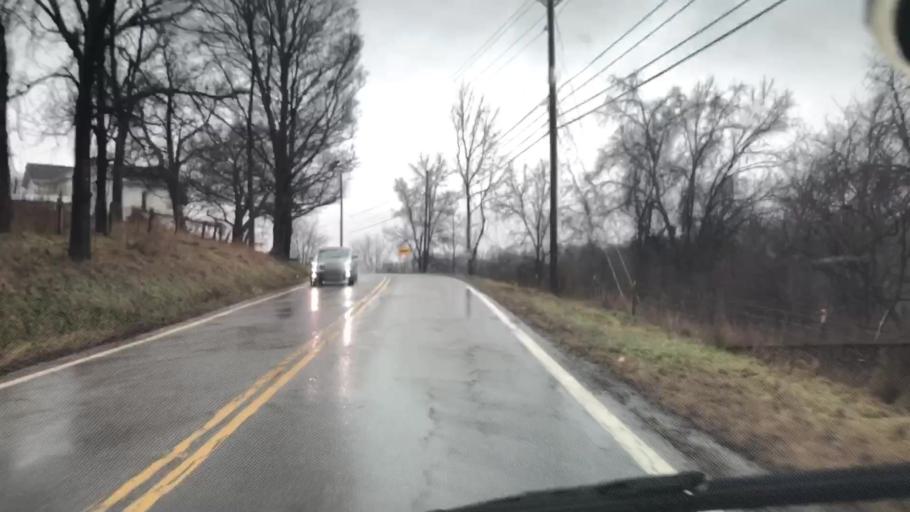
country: US
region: Ohio
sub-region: Harrison County
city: Cadiz
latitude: 40.2591
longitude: -81.0026
